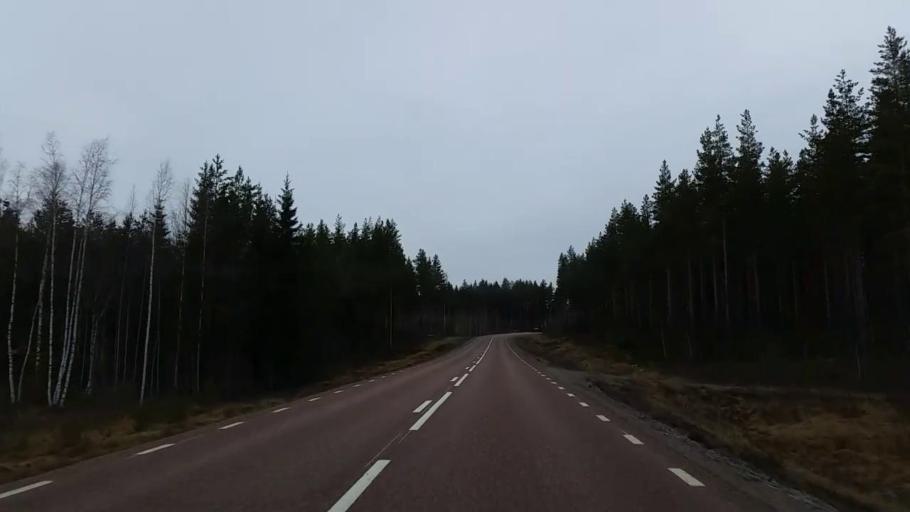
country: SE
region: Gaevleborg
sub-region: Ovanakers Kommun
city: Edsbyn
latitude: 61.2090
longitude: 15.8709
